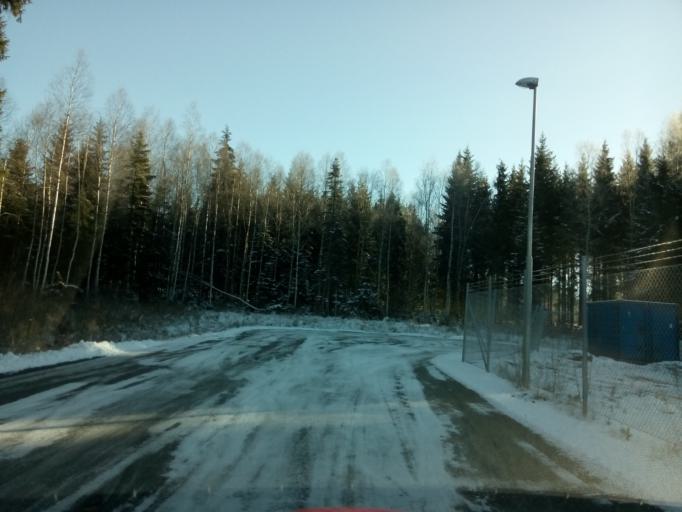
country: SE
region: Vaestra Goetaland
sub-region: Boras Kommun
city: Ganghester
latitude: 57.8347
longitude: 13.0175
